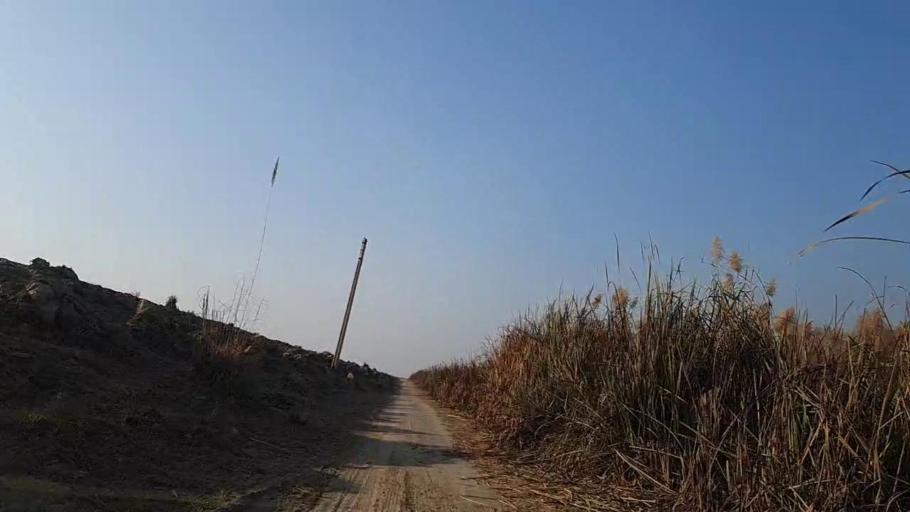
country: PK
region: Sindh
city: Sakrand
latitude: 26.0980
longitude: 68.3695
